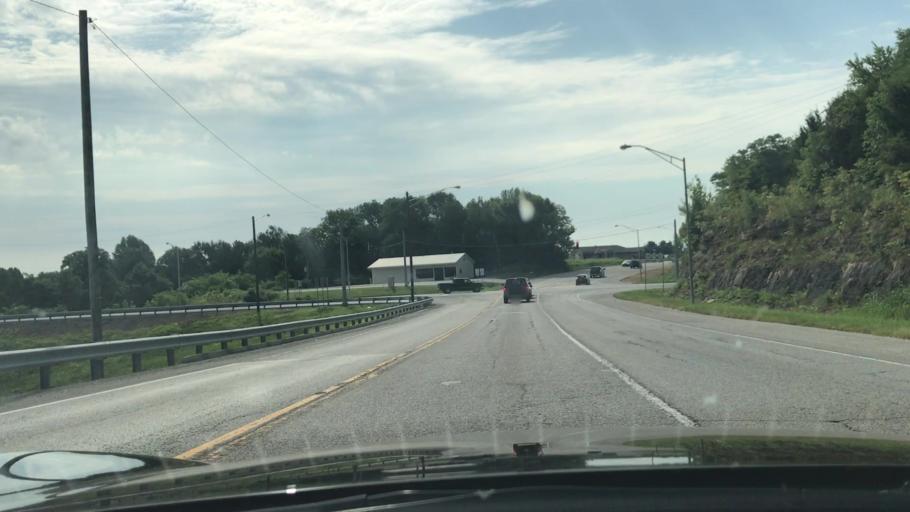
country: US
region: Kentucky
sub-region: Green County
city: Greensburg
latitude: 37.2715
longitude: -85.4972
